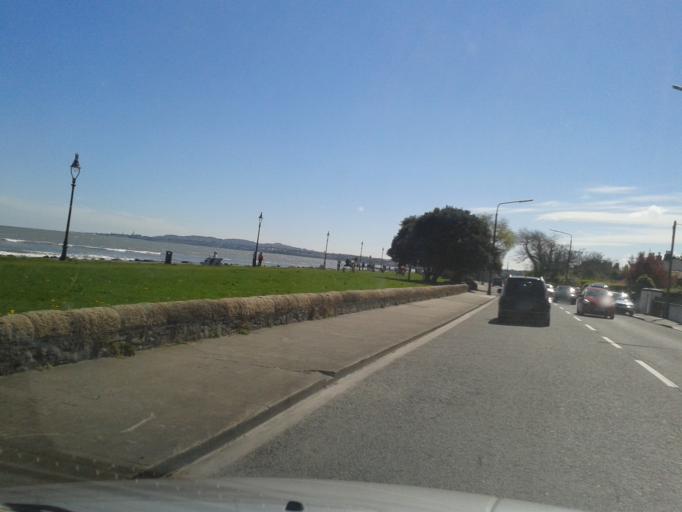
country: IE
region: Leinster
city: Sandymount
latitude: 53.3269
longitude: -6.2082
